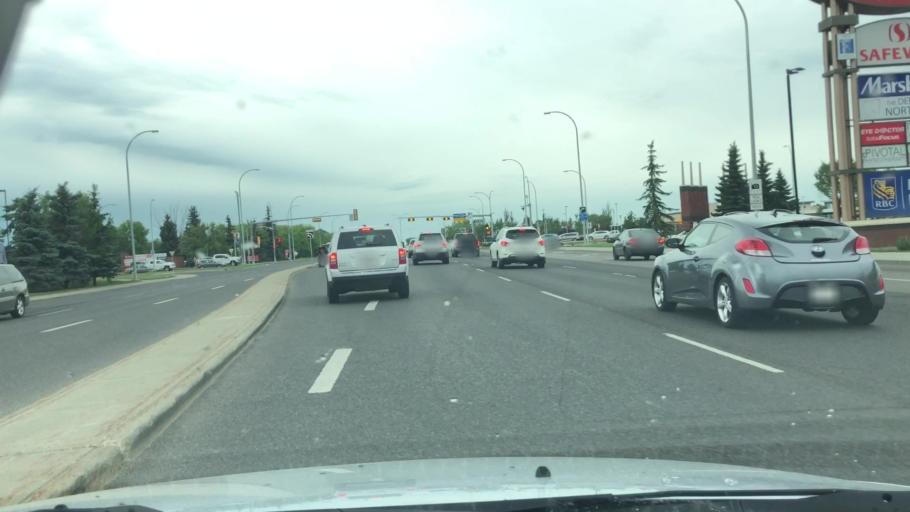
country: CA
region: Alberta
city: Edmonton
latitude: 53.5982
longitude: -113.4919
